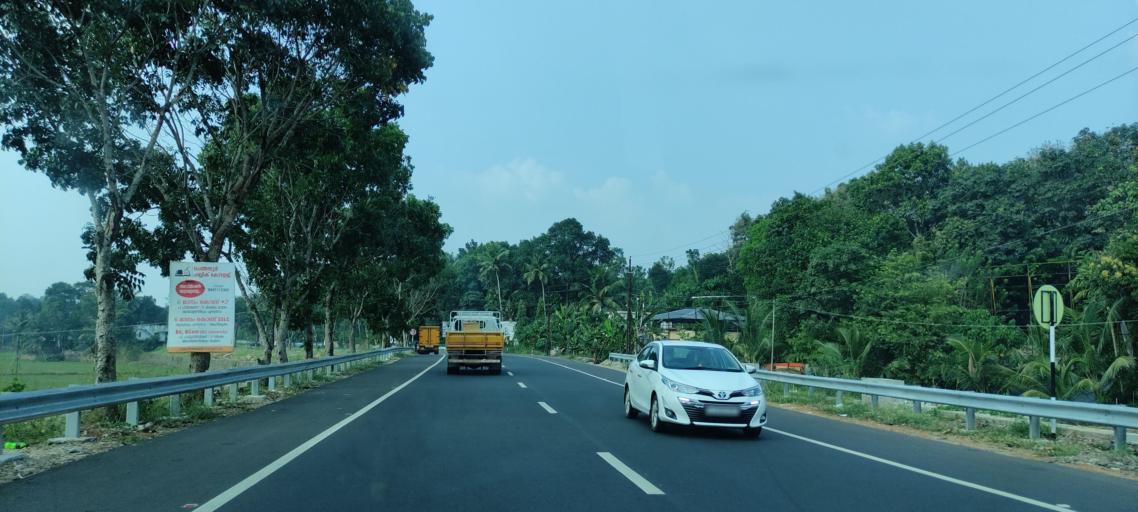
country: IN
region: Kerala
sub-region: Alappuzha
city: Chengannur
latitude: 9.2570
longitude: 76.6600
